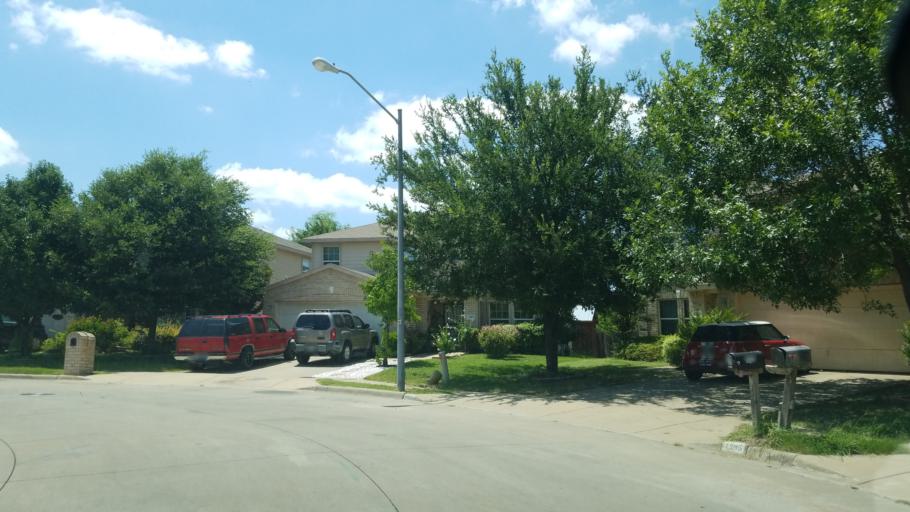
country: US
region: Texas
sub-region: Dallas County
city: Hutchins
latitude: 32.7386
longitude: -96.7125
